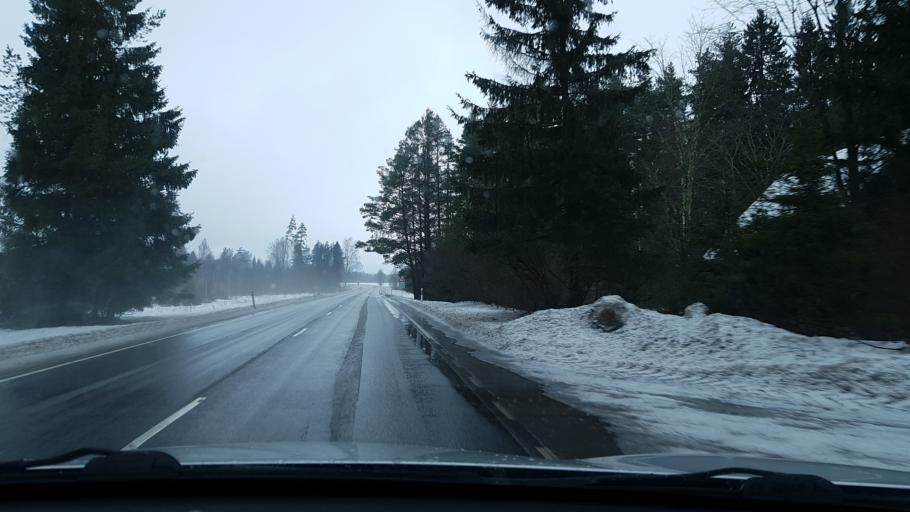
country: EE
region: Raplamaa
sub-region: Kehtna vald
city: Kehtna
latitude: 58.8971
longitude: 24.9036
